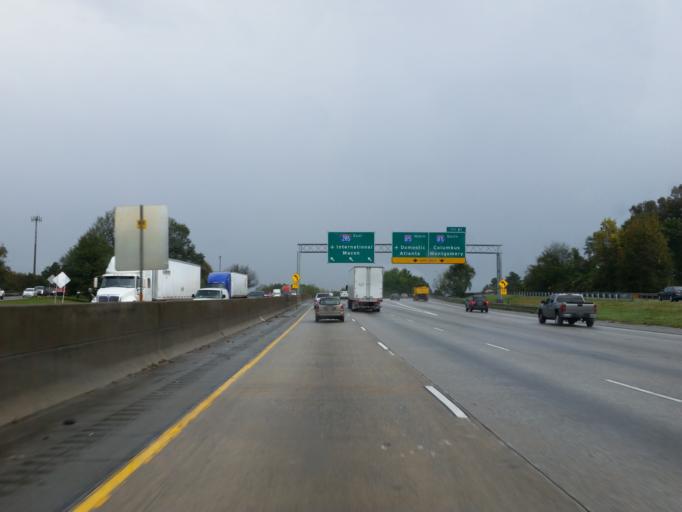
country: US
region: Georgia
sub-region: Fulton County
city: College Park
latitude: 33.6246
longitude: -84.4885
